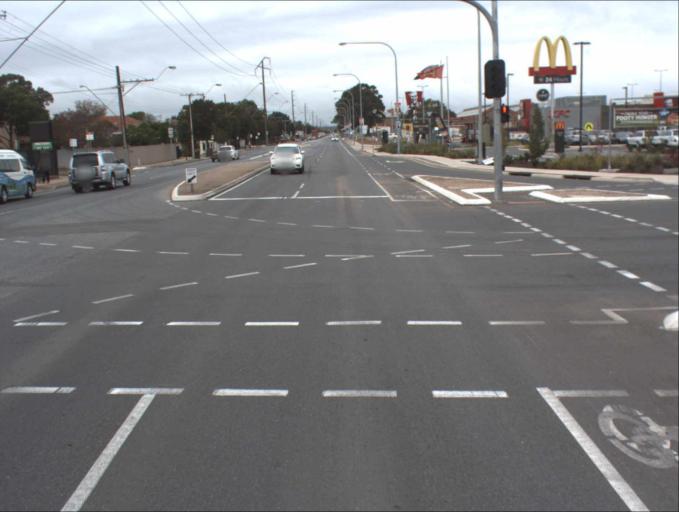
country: AU
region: South Australia
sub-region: Port Adelaide Enfield
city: Blair Athol
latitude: -34.8650
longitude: 138.5834
